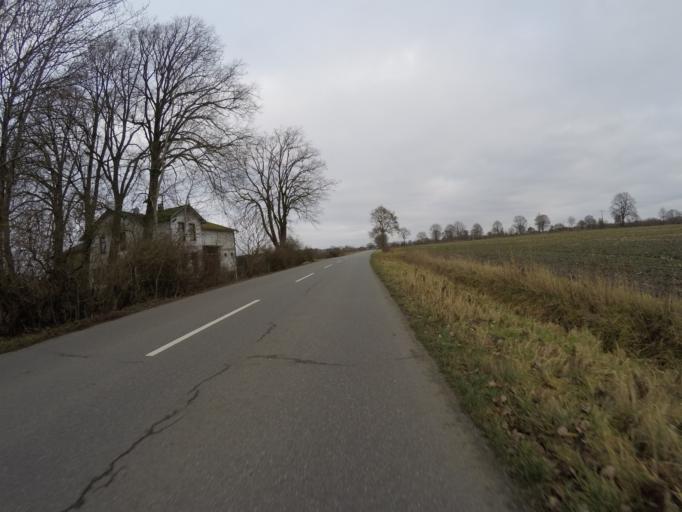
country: DE
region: Schleswig-Holstein
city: Langeln
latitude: 53.7889
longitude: 9.8375
